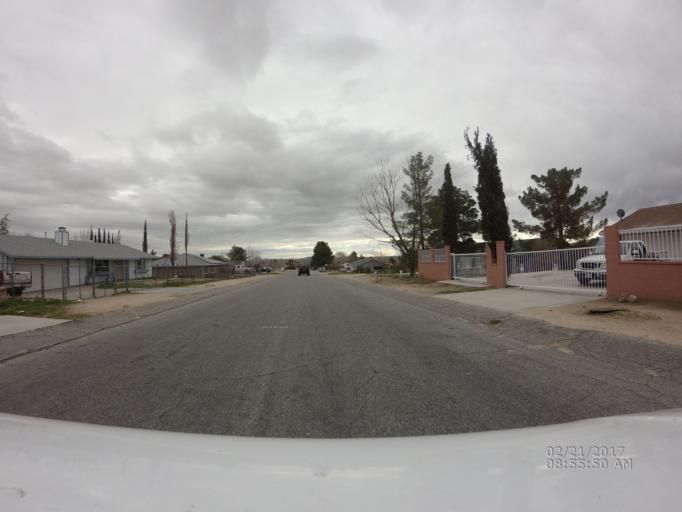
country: US
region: California
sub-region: Los Angeles County
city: Lake Los Angeles
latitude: 34.5954
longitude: -117.8391
